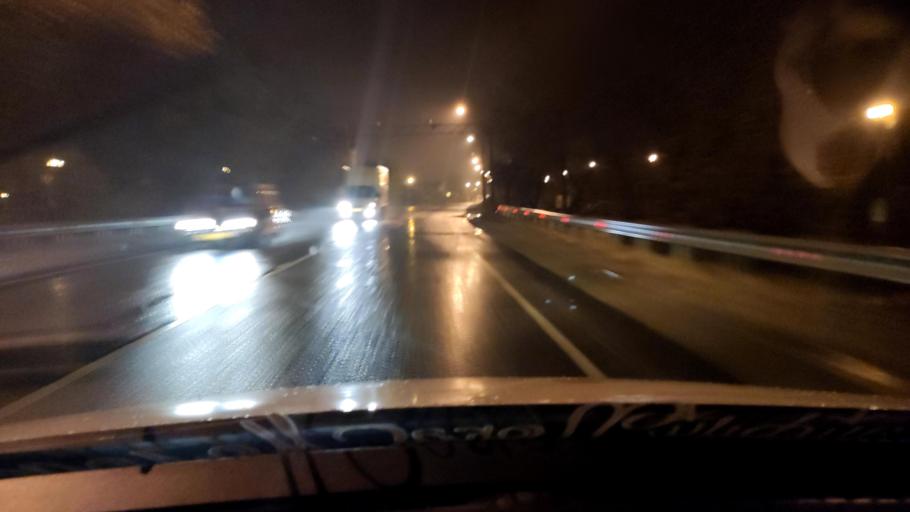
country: RU
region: Voronezj
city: Pridonskoy
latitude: 51.7140
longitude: 39.0748
